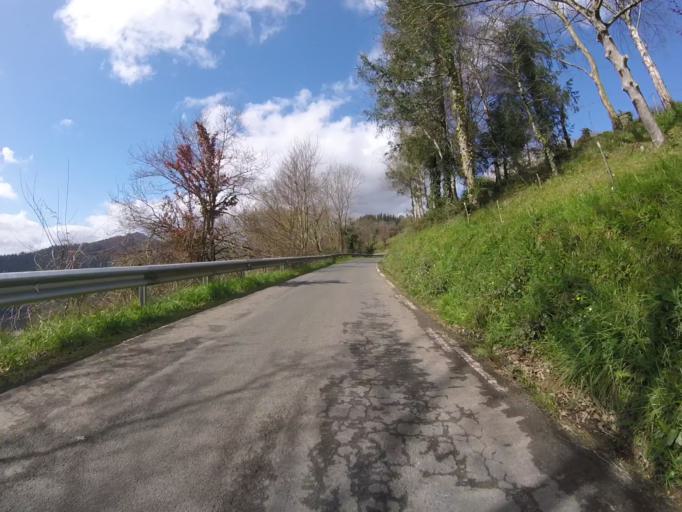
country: ES
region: Basque Country
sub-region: Provincia de Guipuzcoa
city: Tolosa
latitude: 43.1305
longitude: -2.1008
